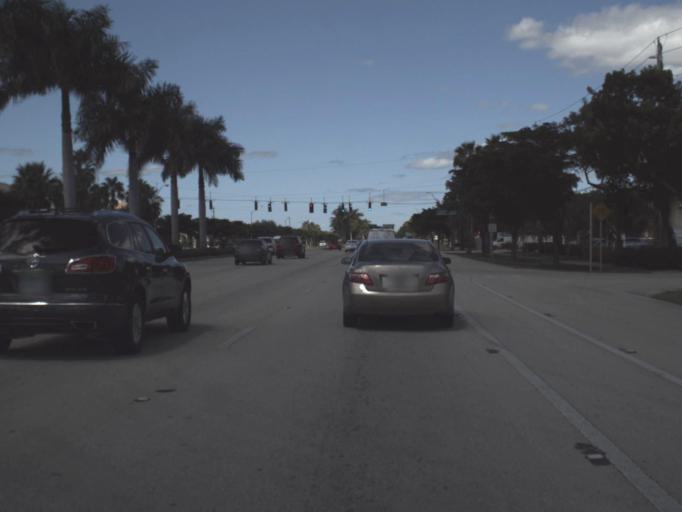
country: US
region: Florida
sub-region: Collier County
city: Lely
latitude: 26.1147
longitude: -81.7546
